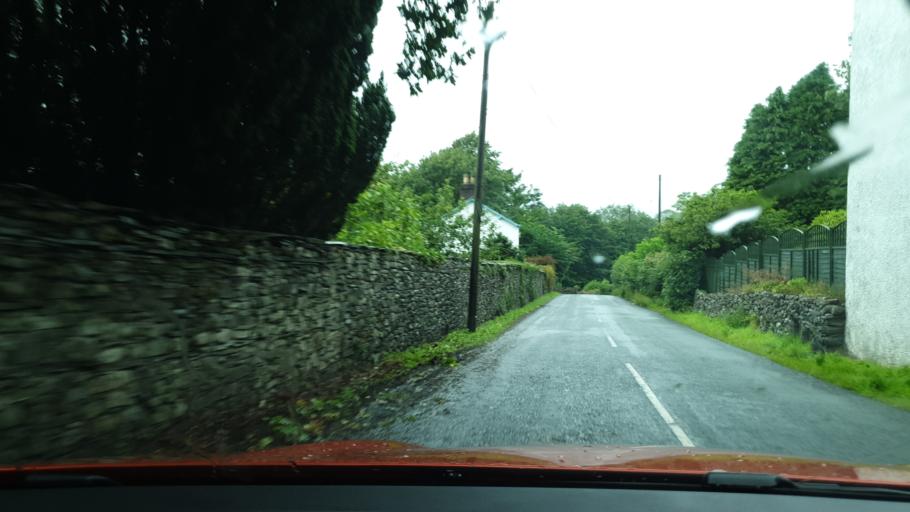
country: GB
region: England
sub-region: Cumbria
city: Ulverston
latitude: 54.2530
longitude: -3.0626
